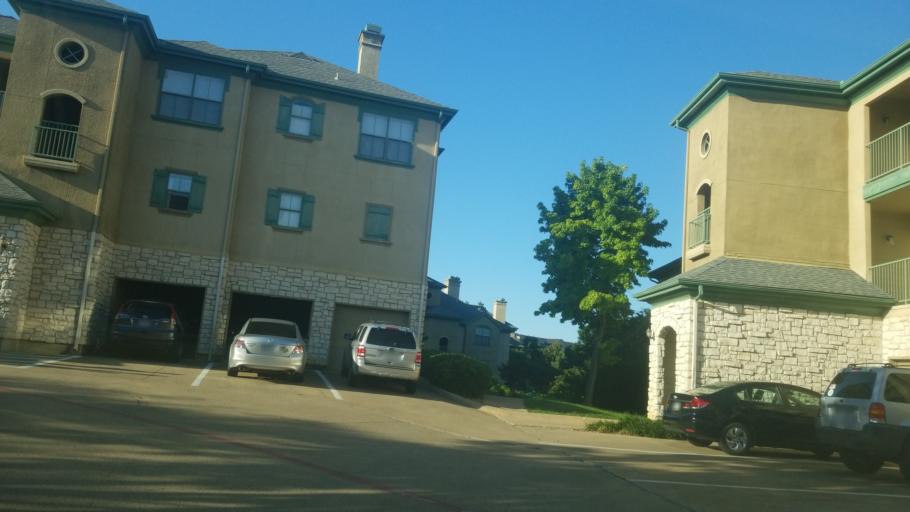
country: US
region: Texas
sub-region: Dallas County
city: Irving
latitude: 32.8817
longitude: -96.9581
